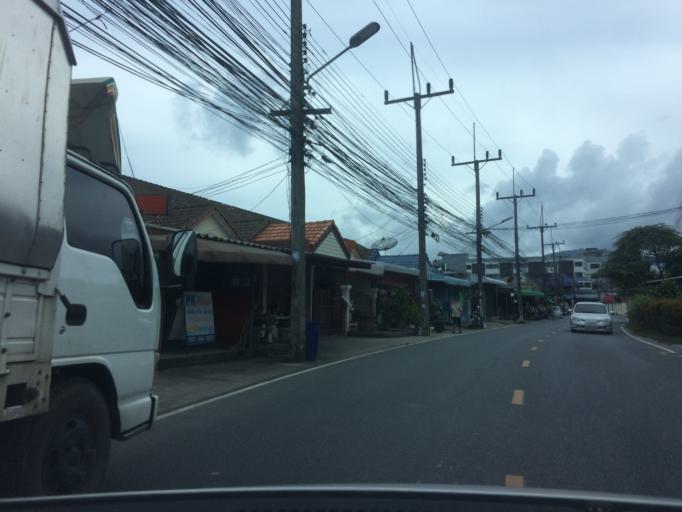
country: TH
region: Phuket
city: Mueang Phuket
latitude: 7.8620
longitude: 98.3615
